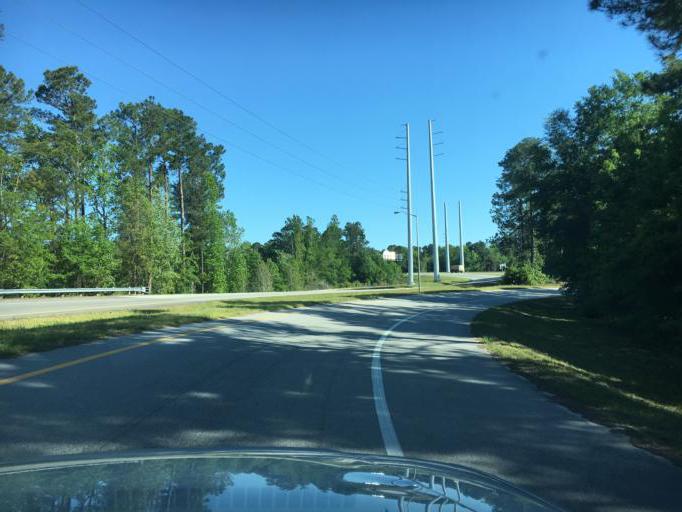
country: US
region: South Carolina
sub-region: Orangeburg County
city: Brookdale
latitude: 33.5582
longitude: -80.8258
